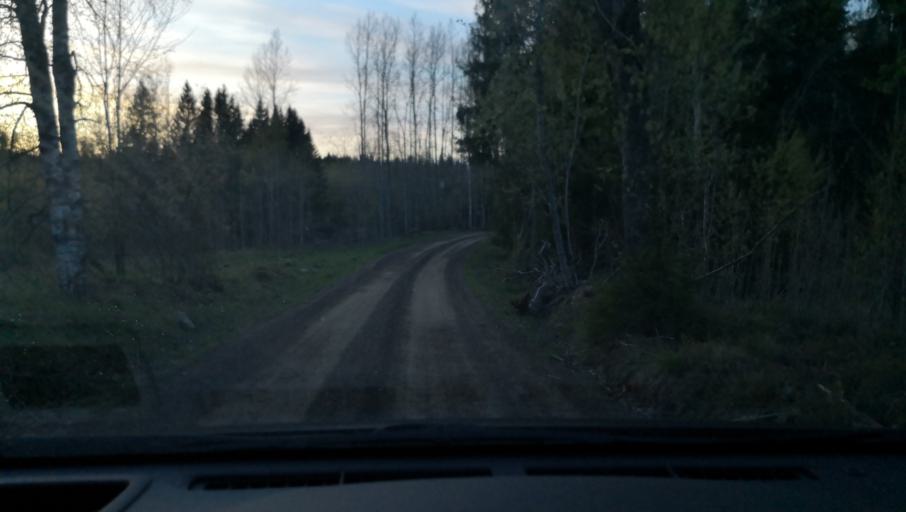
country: SE
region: OErebro
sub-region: Askersunds Kommun
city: Askersund
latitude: 58.9867
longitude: 14.9221
